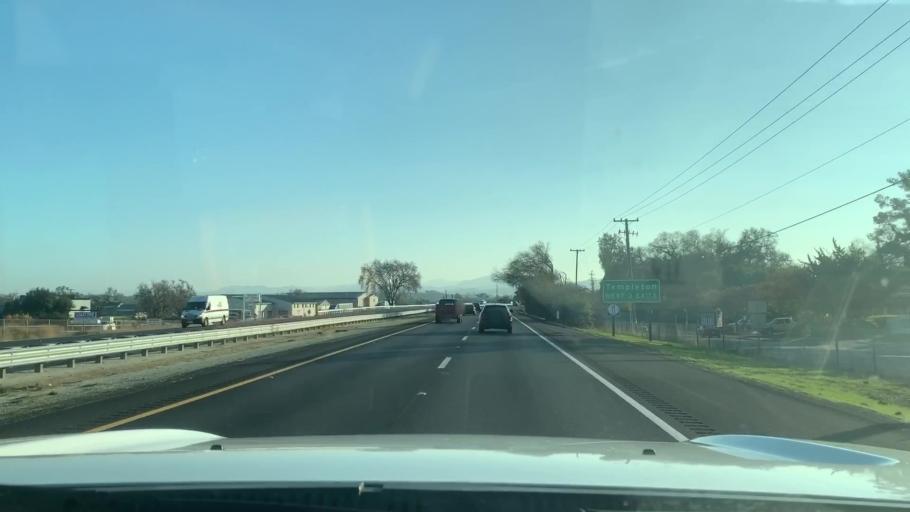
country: US
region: California
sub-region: San Luis Obispo County
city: Templeton
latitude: 35.5770
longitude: -120.6975
